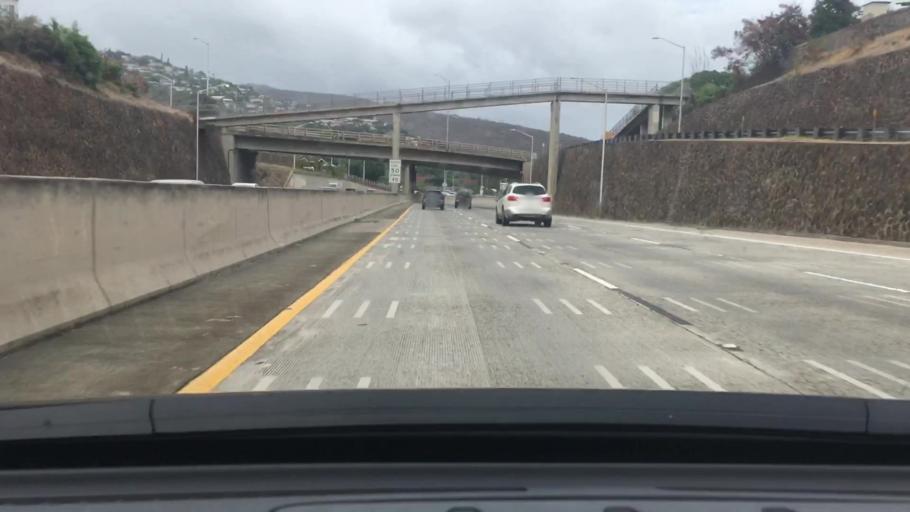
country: US
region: Hawaii
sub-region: Honolulu County
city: Honolulu
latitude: 21.2787
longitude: -157.7931
